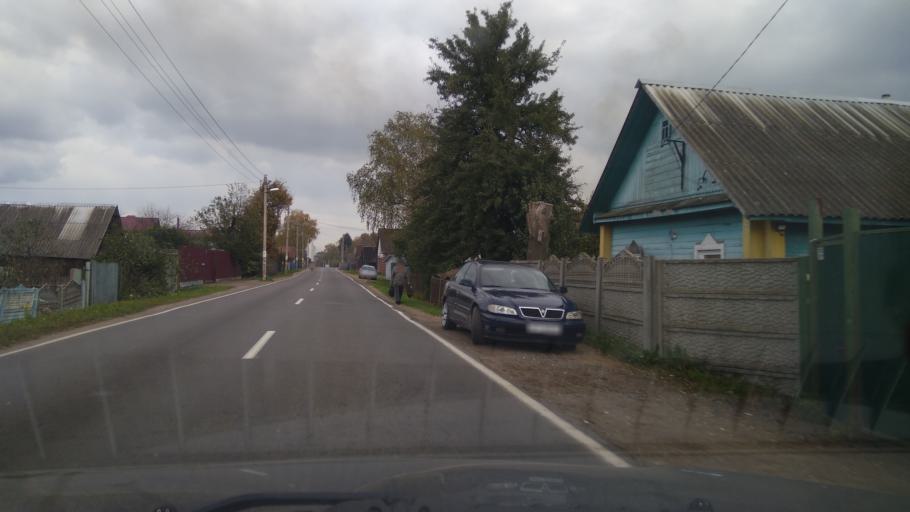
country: BY
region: Minsk
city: Dukora
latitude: 53.6693
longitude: 27.9473
